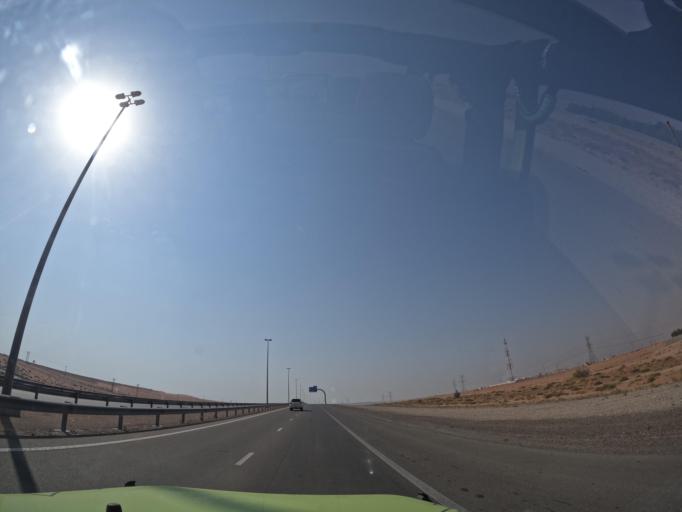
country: OM
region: Al Buraimi
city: Al Buraymi
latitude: 24.3793
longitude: 55.7276
